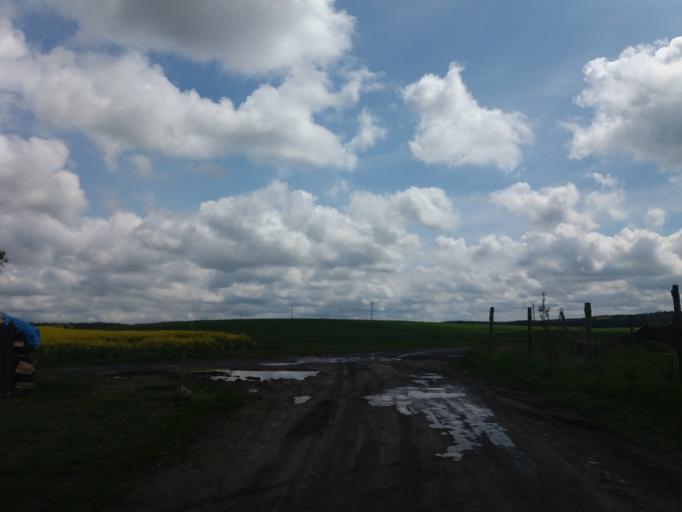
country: PL
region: West Pomeranian Voivodeship
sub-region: Powiat choszczenski
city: Choszczno
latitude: 53.2092
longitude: 15.4001
